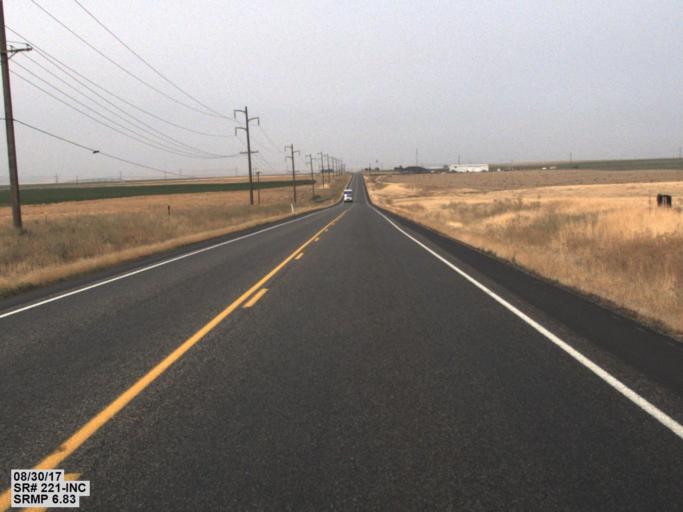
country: US
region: Oregon
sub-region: Morrow County
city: Irrigon
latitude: 46.0341
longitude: -119.6026
